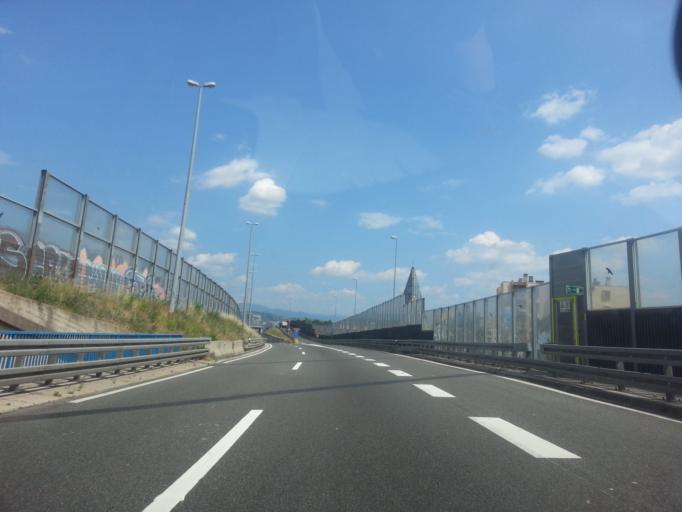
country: HR
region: Primorsko-Goranska
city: Rijeka
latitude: 45.3439
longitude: 14.4000
